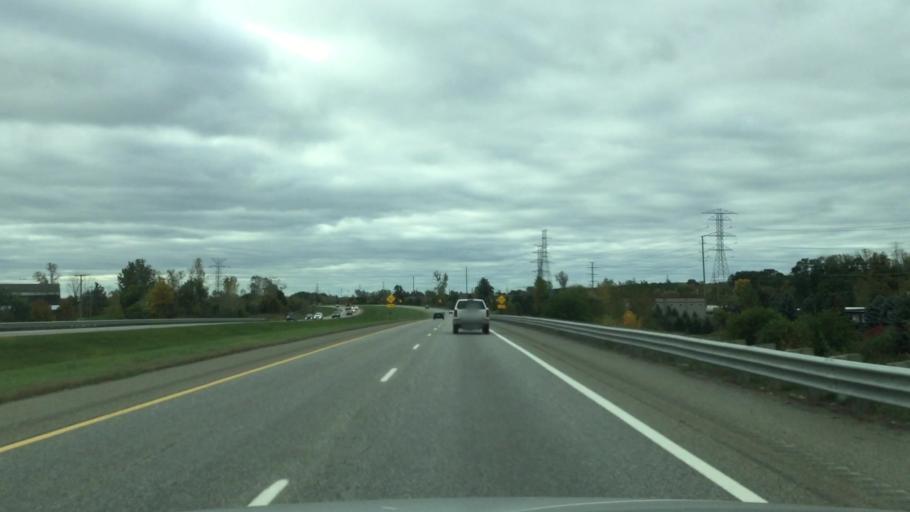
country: US
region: Michigan
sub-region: Macomb County
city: Romeo
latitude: 42.7852
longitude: -83.0067
